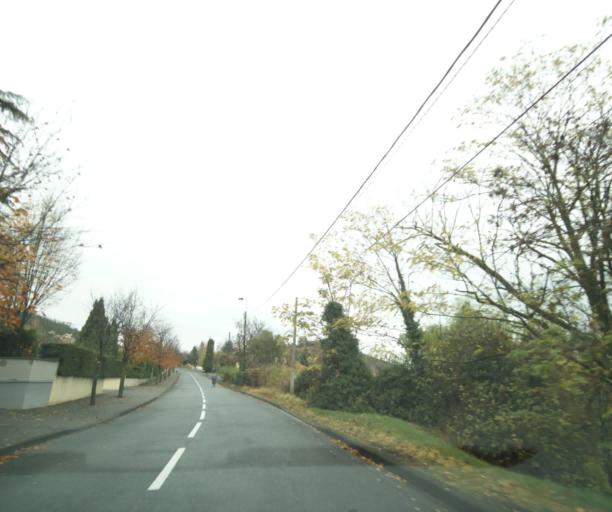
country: FR
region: Auvergne
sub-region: Departement du Puy-de-Dome
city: Cournon-d'Auvergne
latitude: 45.7476
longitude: 3.2031
